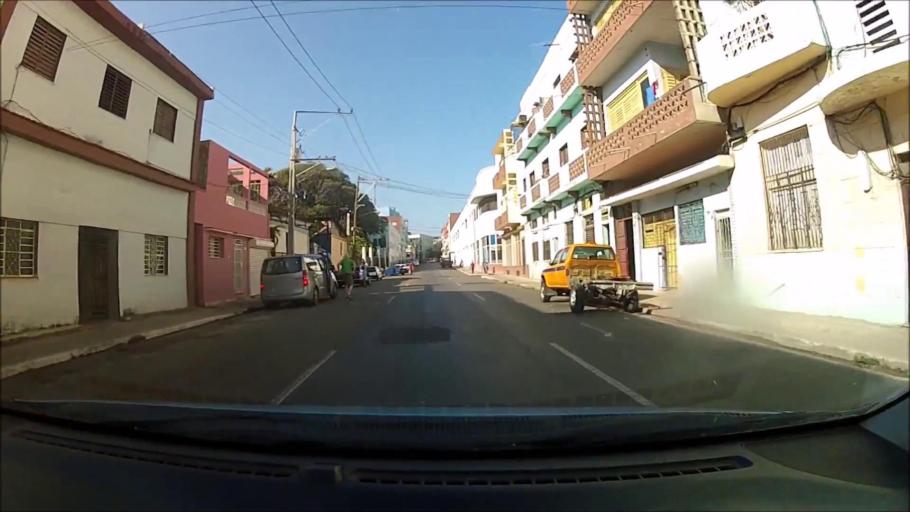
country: CU
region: La Habana
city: Havana
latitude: 23.1425
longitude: -82.3767
